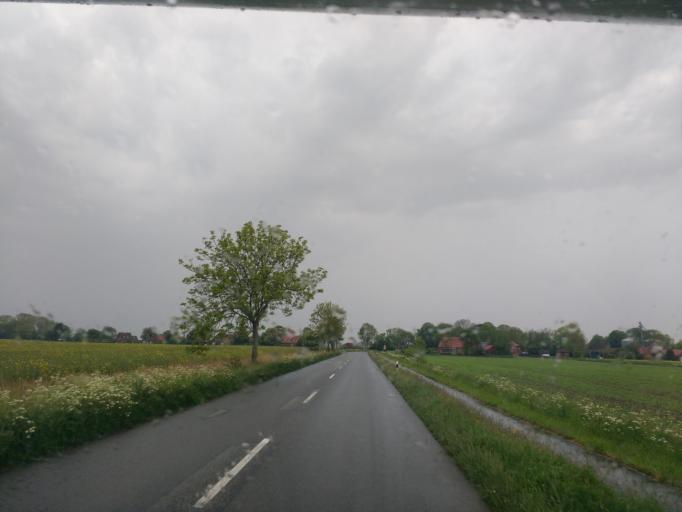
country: DE
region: Lower Saxony
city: Schillig
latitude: 53.6974
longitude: 8.0017
